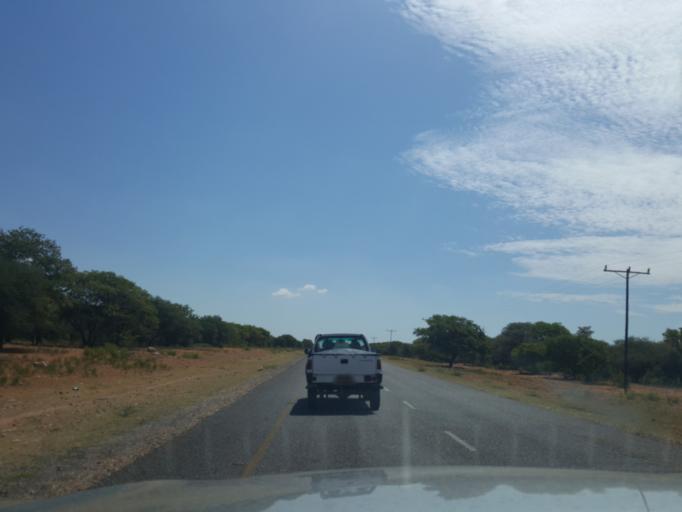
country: BW
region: Kweneng
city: Letlhakeng
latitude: -24.1240
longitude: 25.0979
